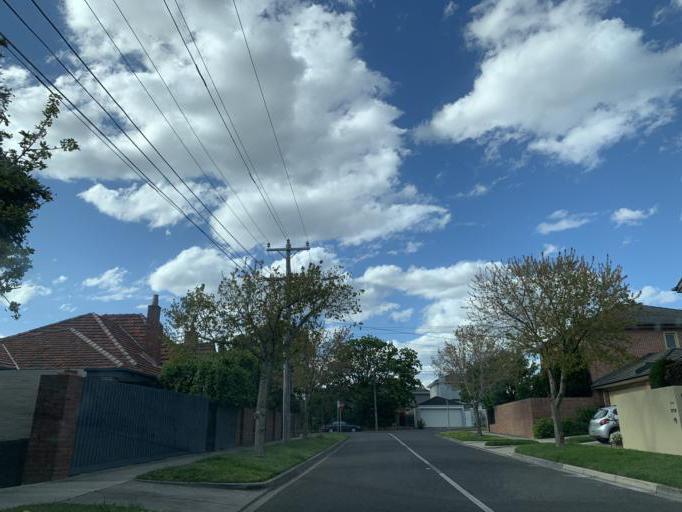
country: AU
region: Victoria
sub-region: Bayside
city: North Brighton
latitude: -37.9221
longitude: 145.0114
